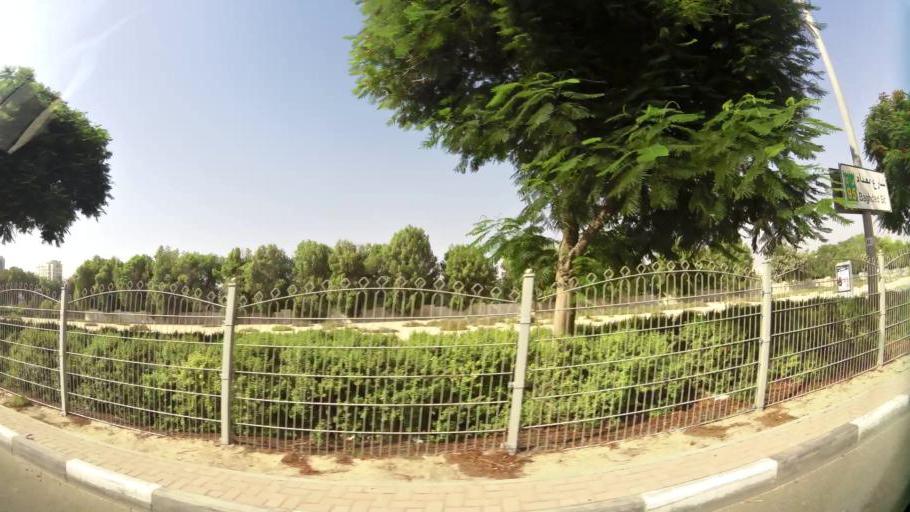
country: AE
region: Ash Shariqah
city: Sharjah
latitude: 25.2836
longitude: 55.3744
